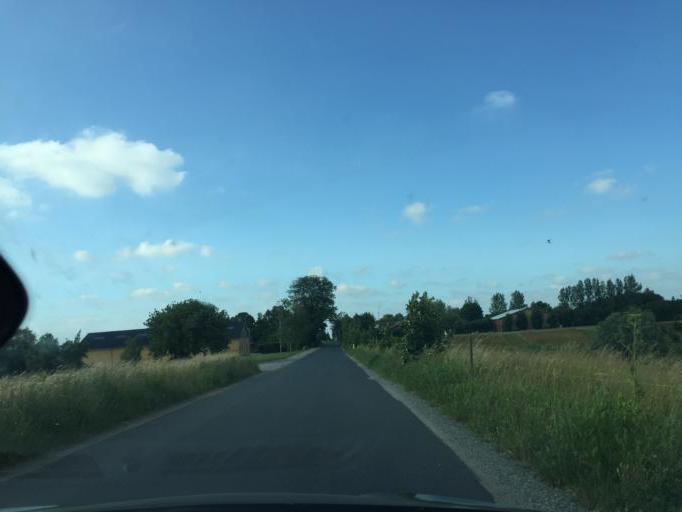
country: DK
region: South Denmark
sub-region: Kerteminde Kommune
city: Langeskov
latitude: 55.3252
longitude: 10.5426
